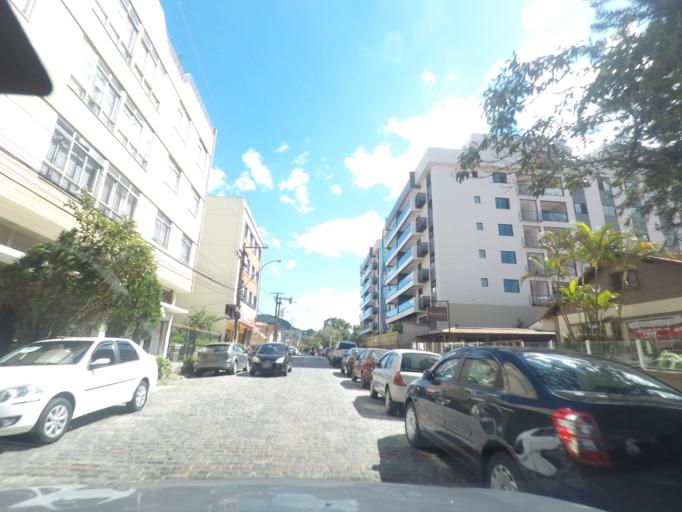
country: BR
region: Rio de Janeiro
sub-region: Teresopolis
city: Teresopolis
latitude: -22.4434
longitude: -42.9786
